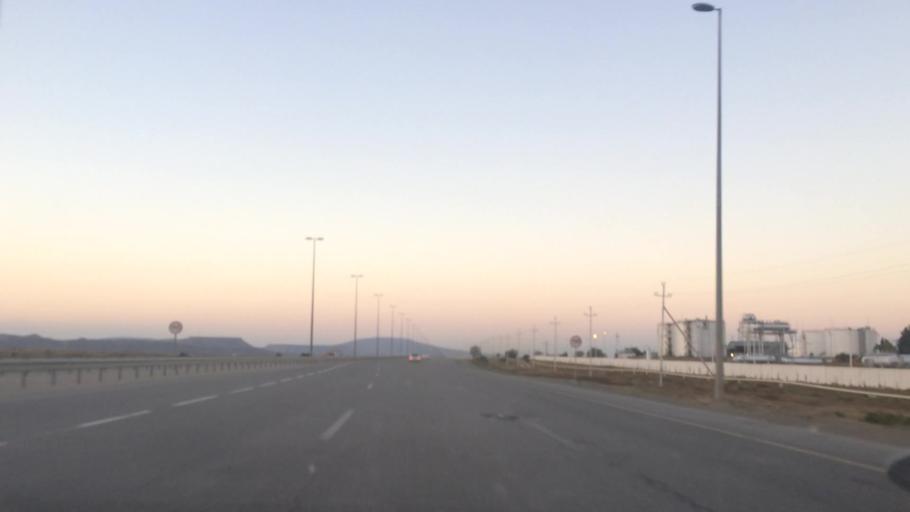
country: AZ
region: Baki
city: Qobustan
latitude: 39.9971
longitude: 49.4308
